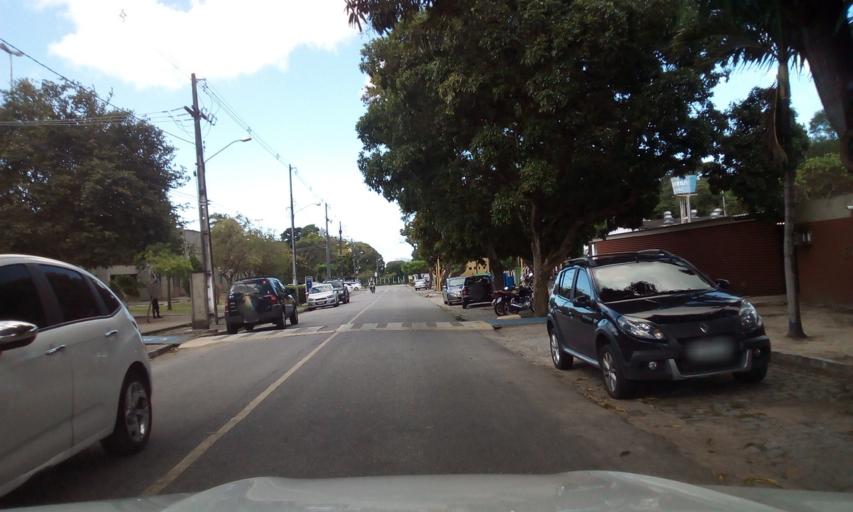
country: BR
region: Paraiba
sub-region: Joao Pessoa
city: Joao Pessoa
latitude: -7.1409
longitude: -34.8468
